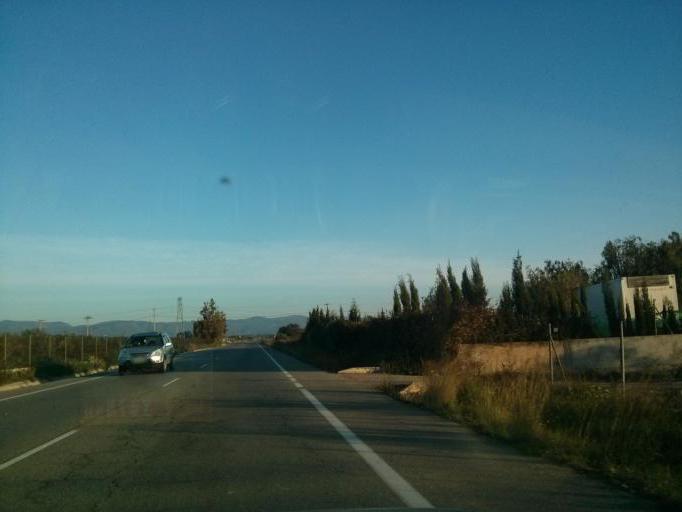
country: ES
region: Catalonia
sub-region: Provincia de Tarragona
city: Santa Oliva
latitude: 41.2430
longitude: 1.5456
